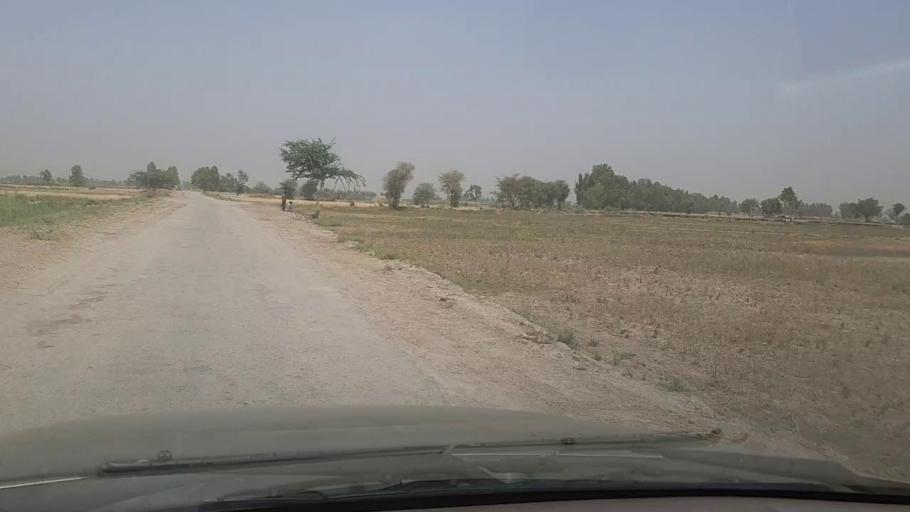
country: PK
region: Sindh
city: Madeji
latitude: 27.8281
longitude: 68.3920
